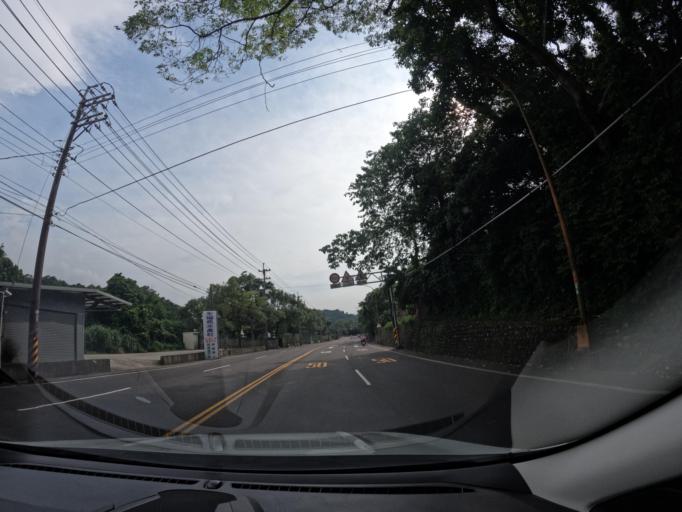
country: TW
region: Taiwan
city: Daxi
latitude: 24.8944
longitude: 121.3101
